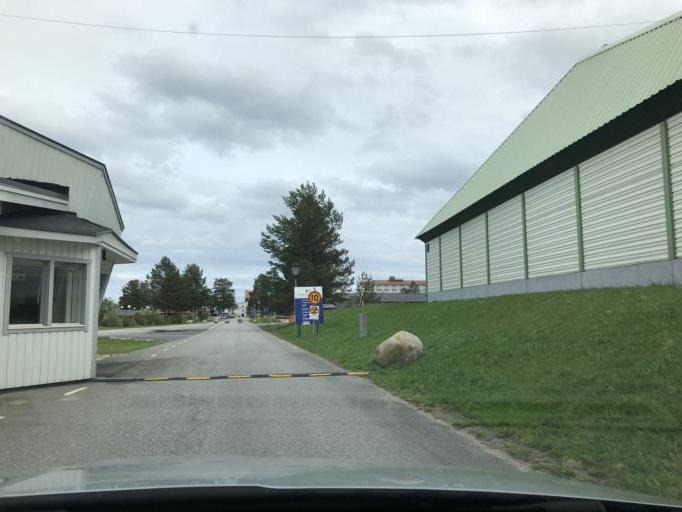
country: SE
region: Norrbotten
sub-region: Pitea Kommun
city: Pitea
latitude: 65.2363
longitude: 21.5298
